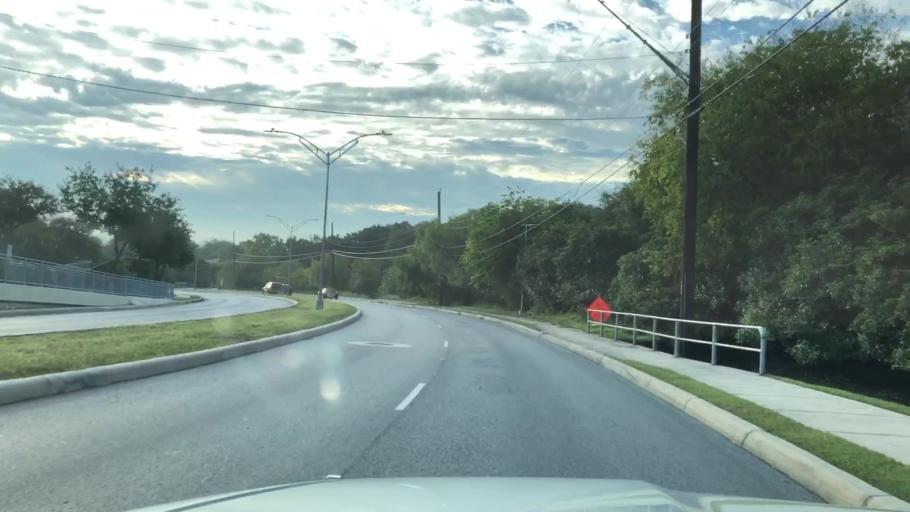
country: US
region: Texas
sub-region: Bexar County
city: Leon Valley
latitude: 29.5425
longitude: -98.6370
